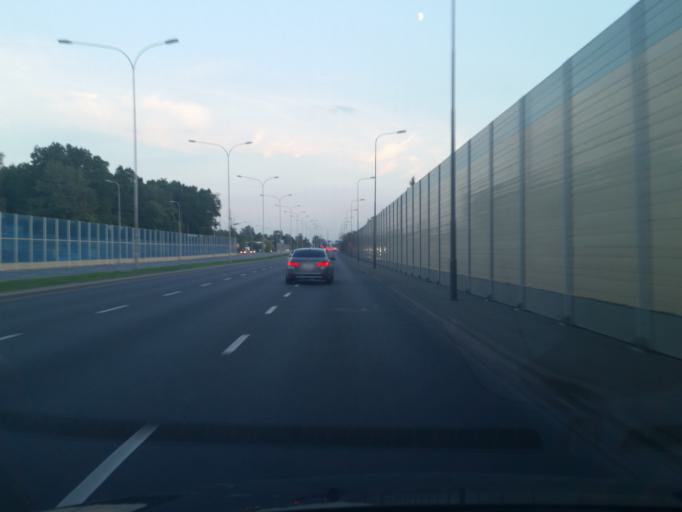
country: PL
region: Masovian Voivodeship
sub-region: Powiat legionowski
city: Jablonna
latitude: 52.3545
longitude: 20.9422
